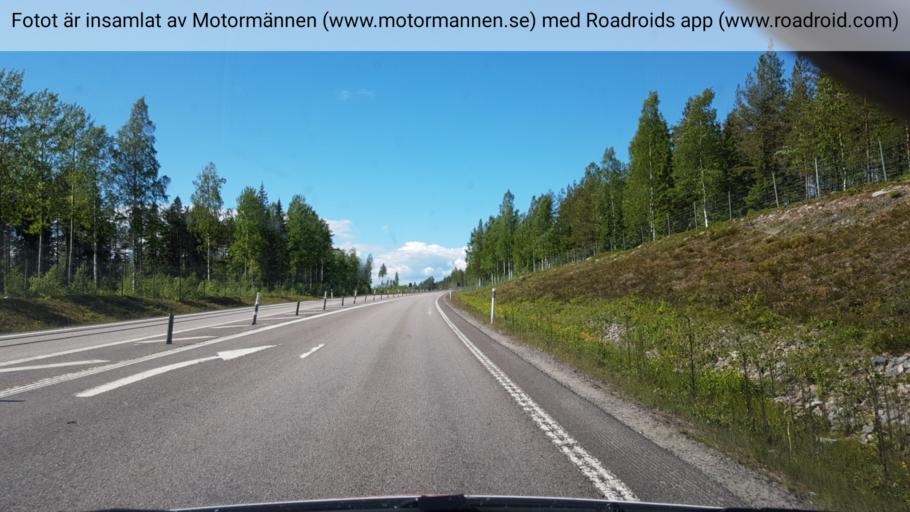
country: SE
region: Norrbotten
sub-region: Kalix Kommun
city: Toere
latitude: 65.9055
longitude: 22.8429
